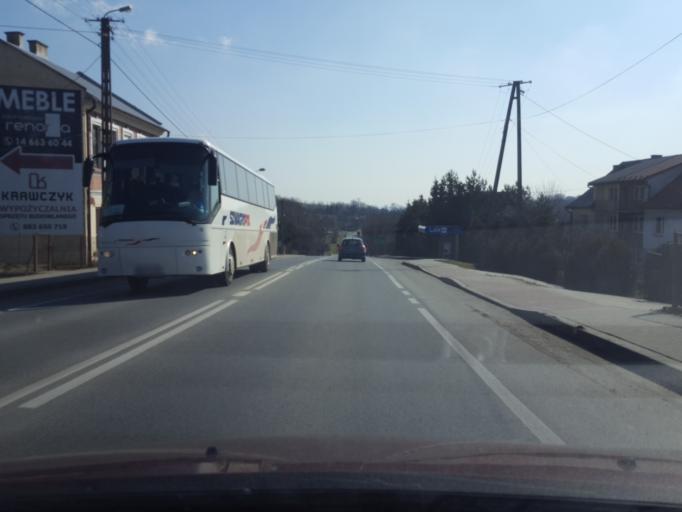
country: PL
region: Lesser Poland Voivodeship
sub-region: Powiat brzeski
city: Gnojnik
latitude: 49.8542
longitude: 20.6347
